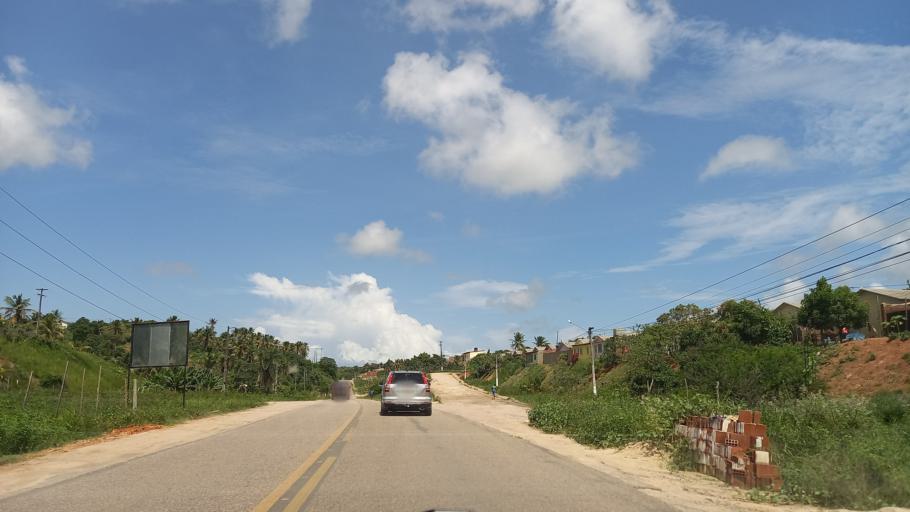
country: BR
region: Pernambuco
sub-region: Barreiros
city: Barreiros
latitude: -8.8197
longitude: -35.1808
